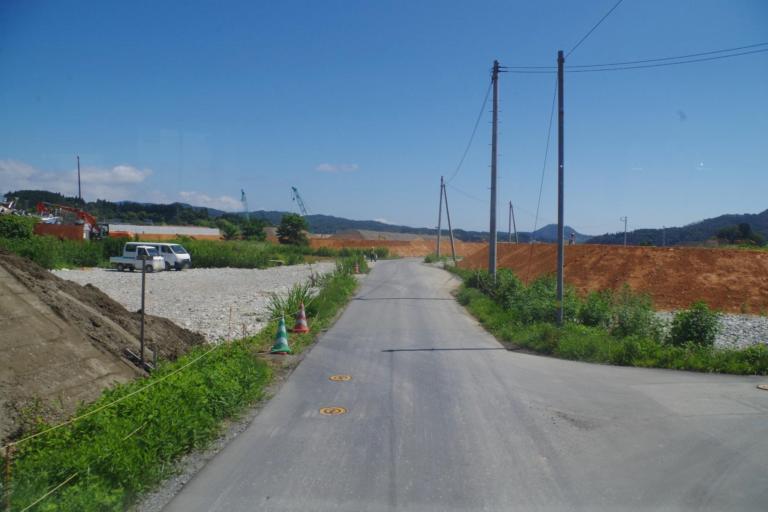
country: JP
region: Iwate
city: Ofunato
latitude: 38.8688
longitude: 141.5825
